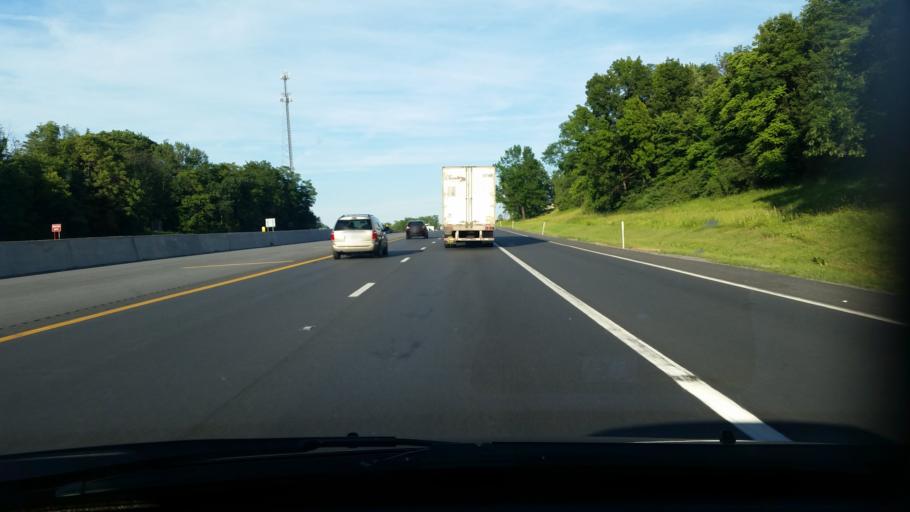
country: US
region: Maryland
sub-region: Washington County
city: Williamsport
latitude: 39.5800
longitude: -77.8729
